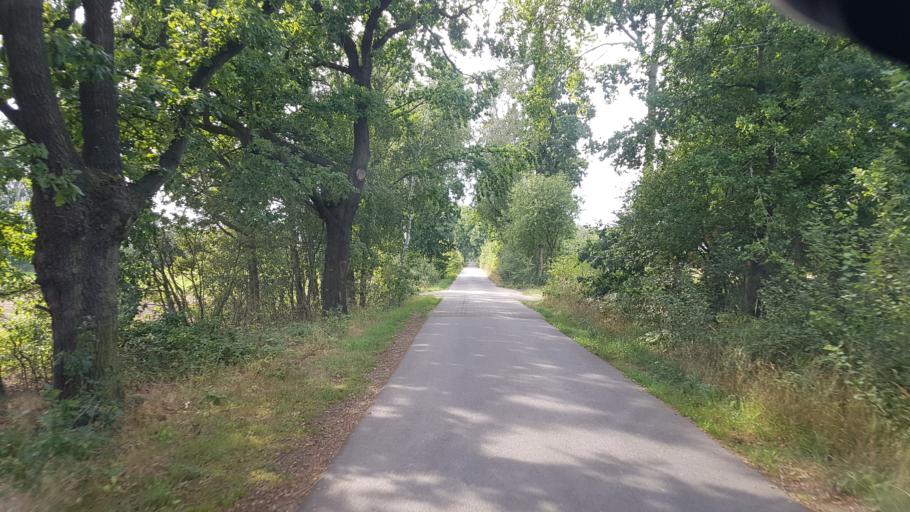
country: DE
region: Brandenburg
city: Plessa
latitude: 51.4400
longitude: 13.6110
